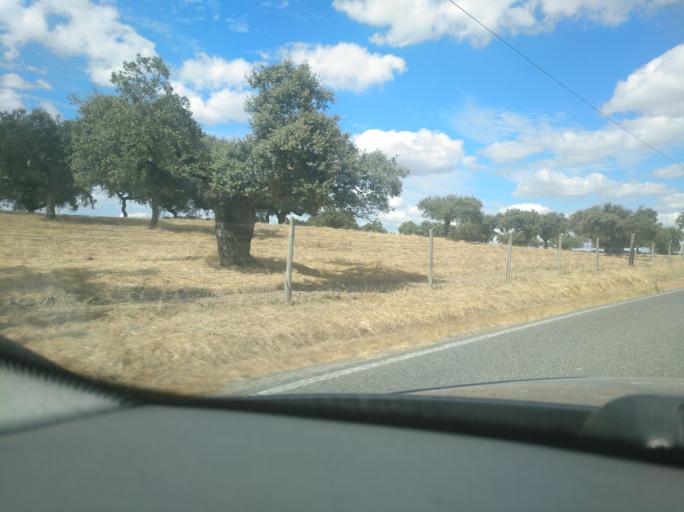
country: PT
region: Portalegre
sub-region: Arronches
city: Arronches
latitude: 39.0901
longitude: -7.3441
